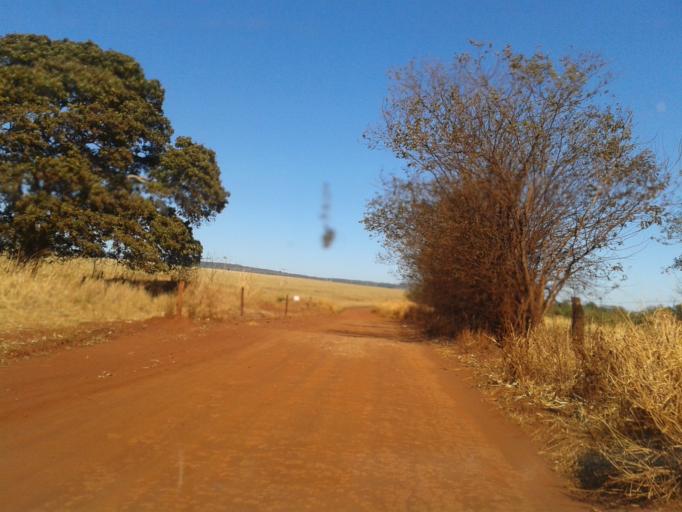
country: BR
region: Minas Gerais
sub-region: Centralina
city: Centralina
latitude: -18.5876
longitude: -49.1485
